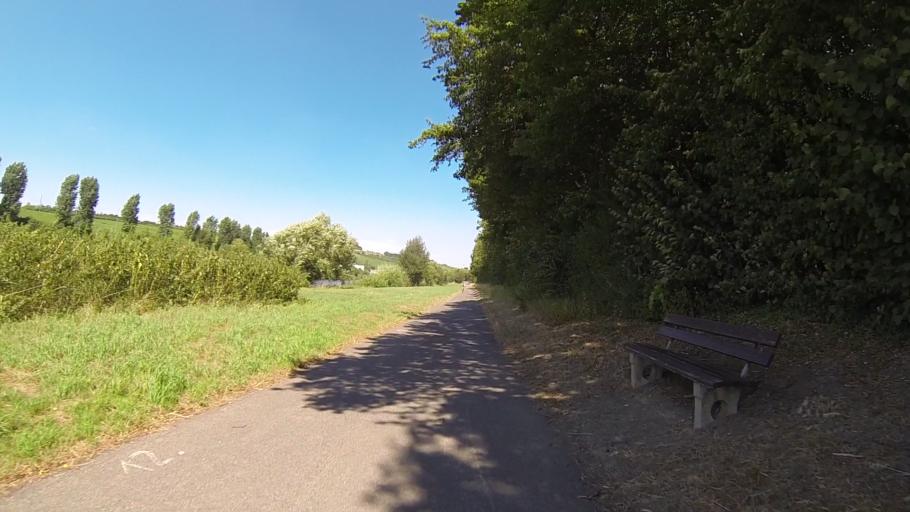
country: DE
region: Rheinland-Pfalz
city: Temmels
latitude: 49.6854
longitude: 6.4553
